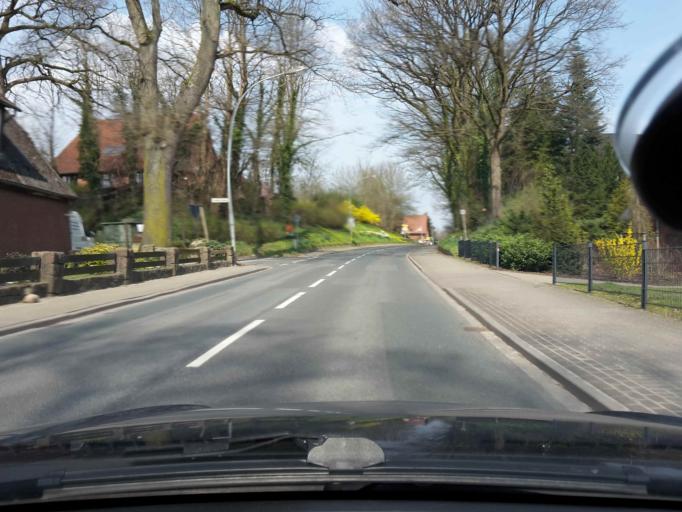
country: DE
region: Lower Saxony
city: Harmstorf
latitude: 53.3654
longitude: 9.9828
